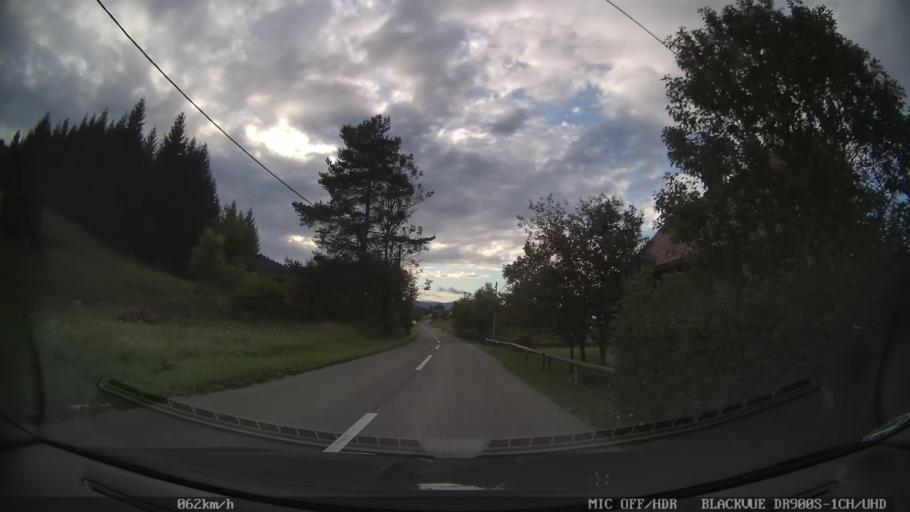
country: HR
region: Licko-Senjska
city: Jezerce
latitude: 44.9707
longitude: 15.5067
